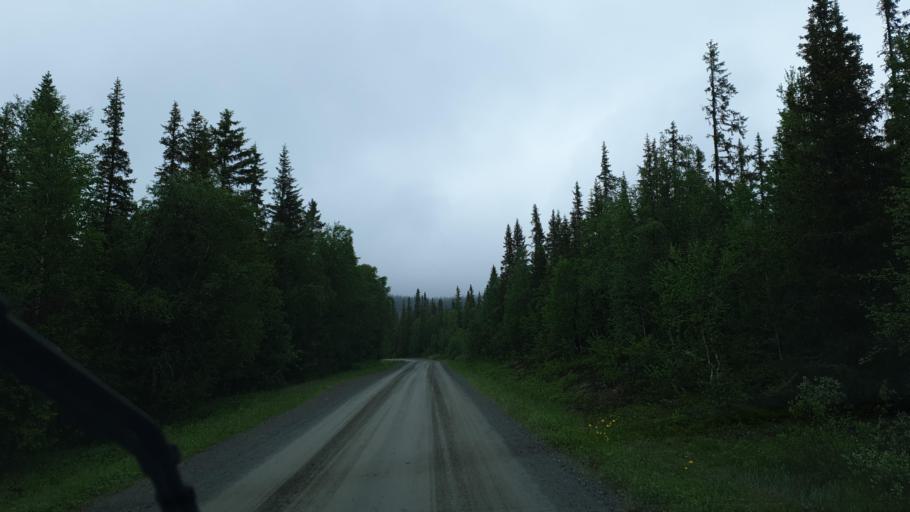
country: SE
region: Vaesterbotten
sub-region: Vilhelmina Kommun
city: Sjoberg
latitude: 65.3377
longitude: 15.8737
